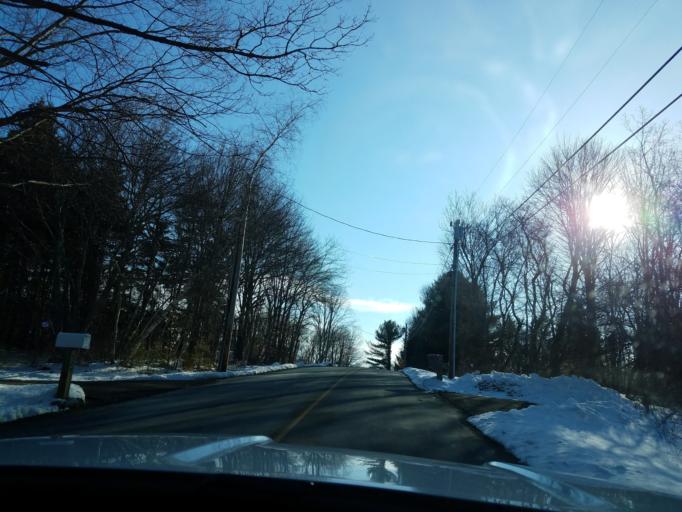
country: US
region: Connecticut
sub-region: Litchfield County
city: Bethlehem Village
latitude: 41.6286
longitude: -73.2461
